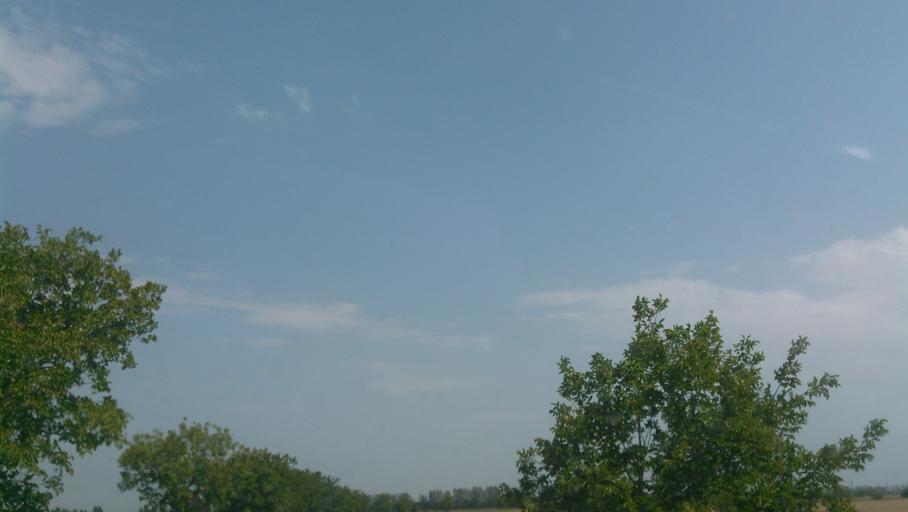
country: SK
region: Trnavsky
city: Dunajska Streda
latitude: 48.0318
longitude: 17.5465
